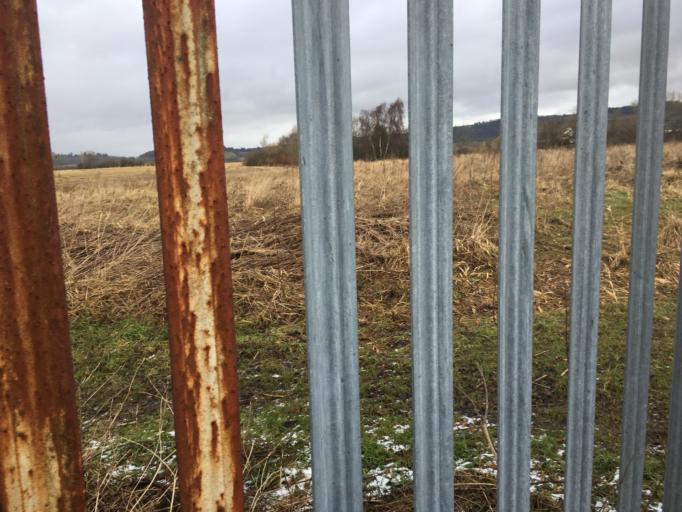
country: GB
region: Scotland
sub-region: Stirling
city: Bridge of Allan
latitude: 56.1364
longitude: -3.9701
